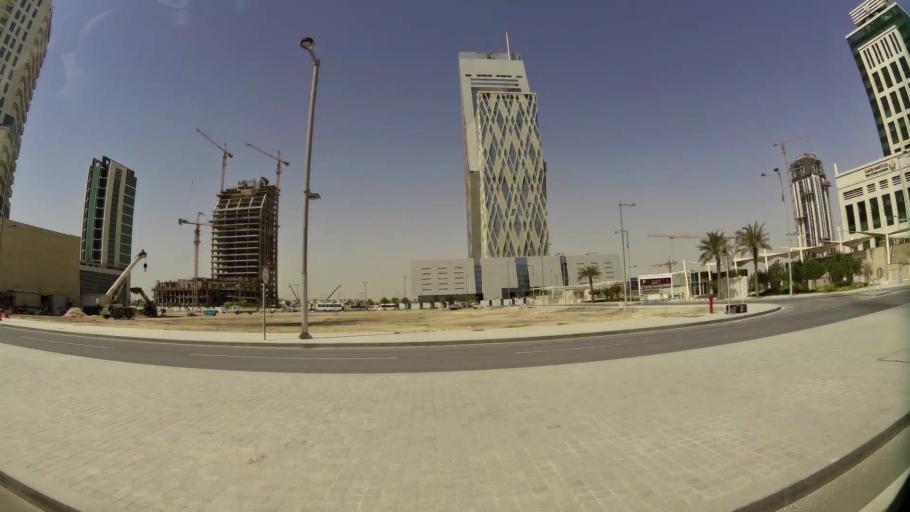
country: QA
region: Baladiyat ad Dawhah
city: Doha
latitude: 25.3920
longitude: 51.5226
